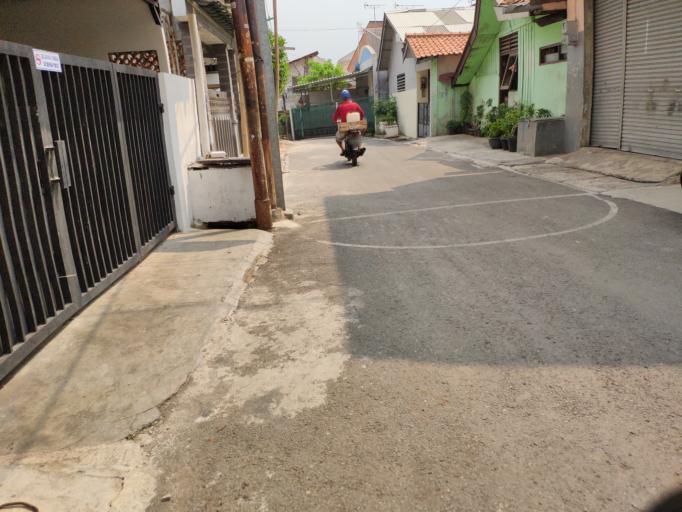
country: ID
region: Jakarta Raya
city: Jakarta
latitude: -6.1962
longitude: 106.8656
